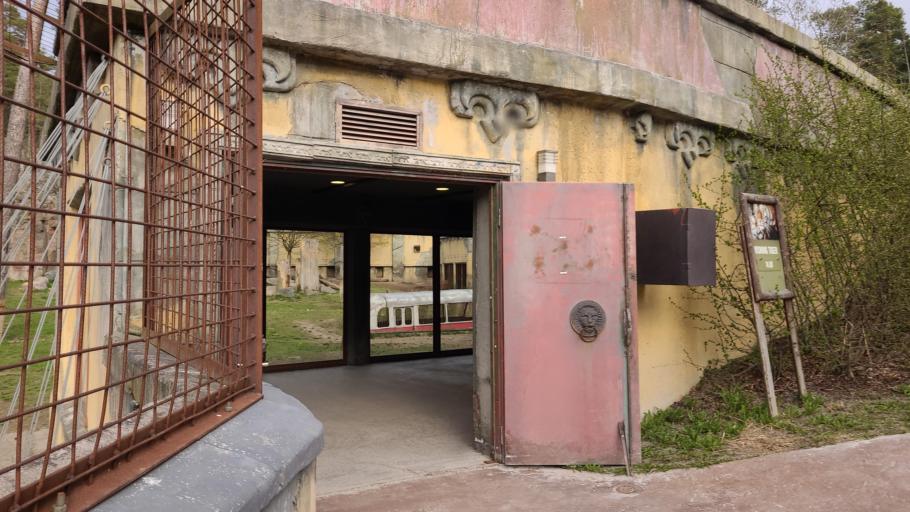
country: SE
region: OEstergoetland
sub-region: Norrkopings Kommun
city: Krokek
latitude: 58.6614
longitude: 16.4504
